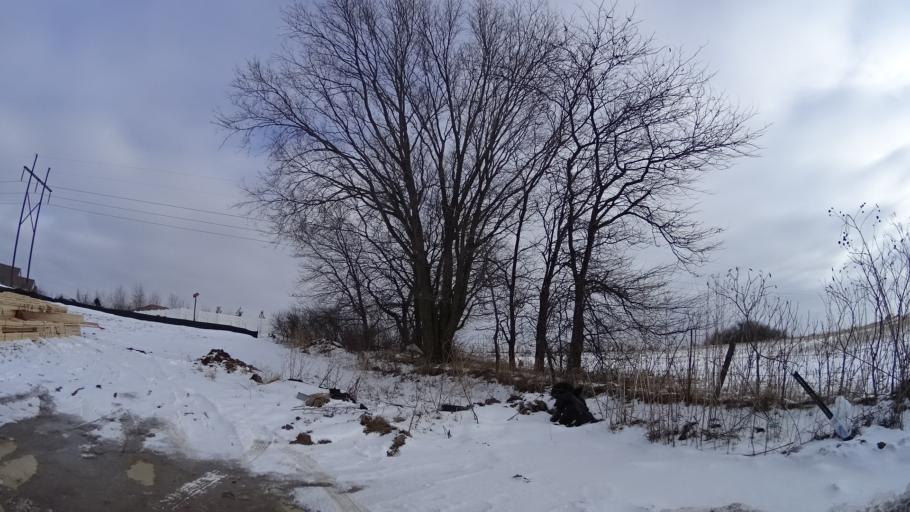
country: US
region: Nebraska
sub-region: Sarpy County
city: Offutt Air Force Base
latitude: 41.1037
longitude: -95.9768
